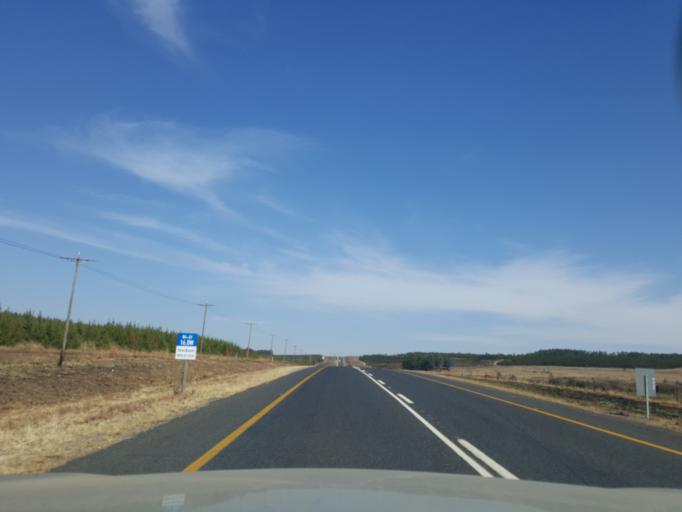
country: ZA
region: Mpumalanga
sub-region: Nkangala District Municipality
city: Belfast
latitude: -25.5163
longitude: 30.3531
